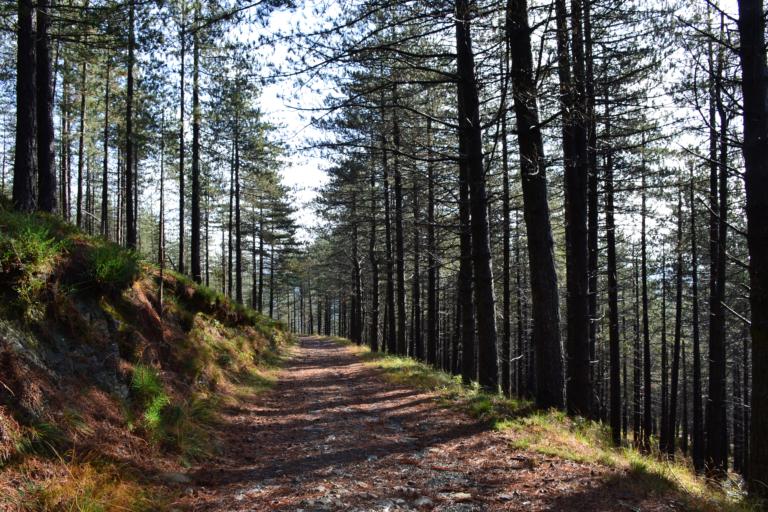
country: PT
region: Vila Real
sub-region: Mondim de Basto
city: Mondim de Basto
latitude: 41.3061
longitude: -7.8982
